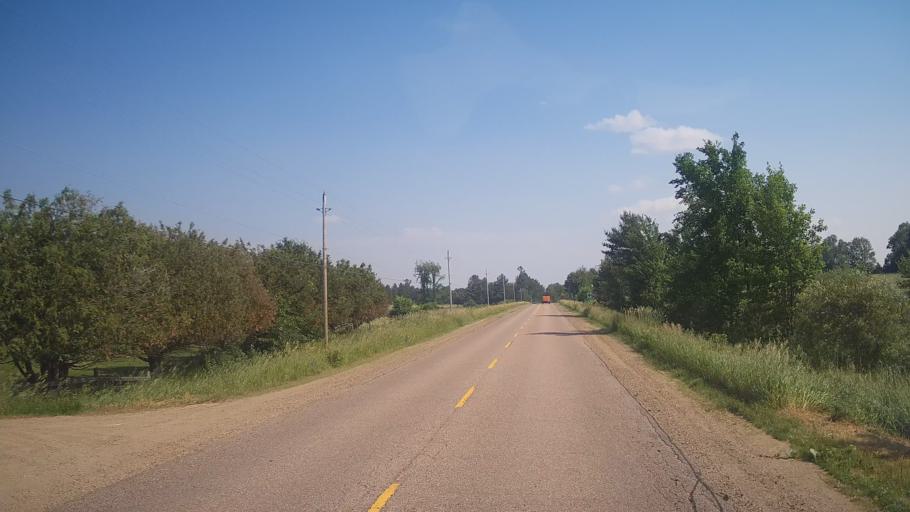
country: CA
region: Ontario
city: Pembroke
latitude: 45.5920
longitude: -77.2285
